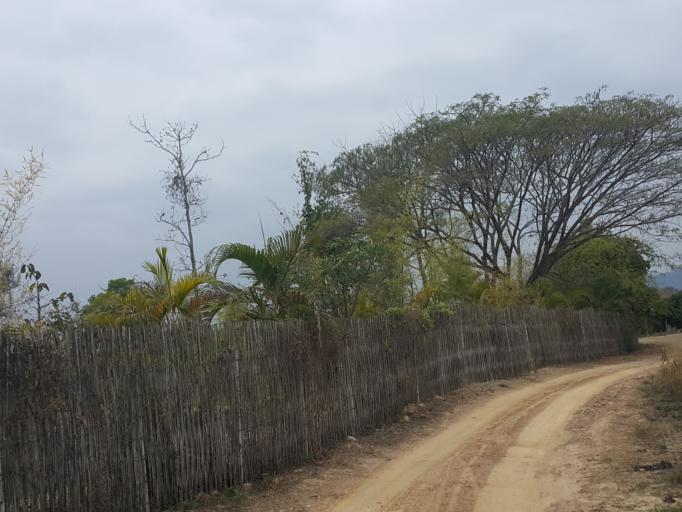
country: TH
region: Chiang Mai
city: Hang Dong
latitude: 18.7042
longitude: 98.8748
